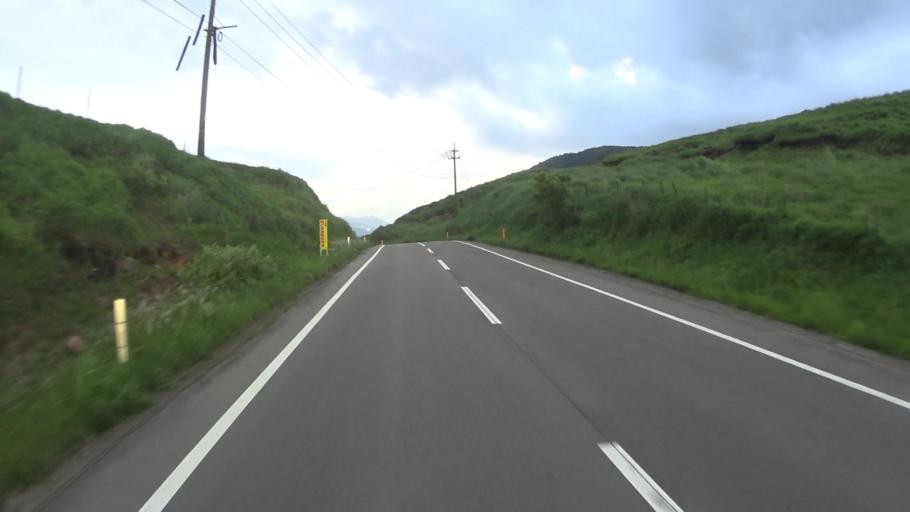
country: JP
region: Kumamoto
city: Ozu
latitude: 32.9122
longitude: 130.9676
